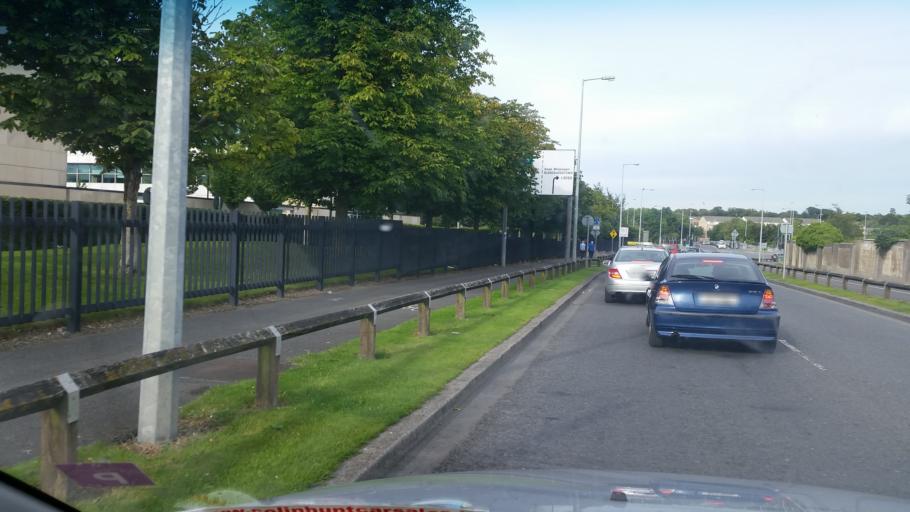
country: IE
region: Leinster
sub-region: Fingal County
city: Blanchardstown
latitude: 53.3906
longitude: -6.3842
